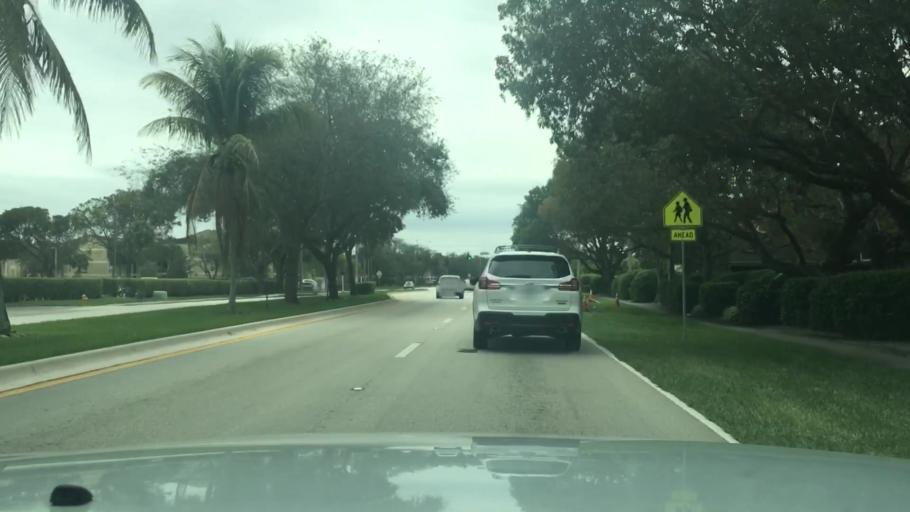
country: US
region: Florida
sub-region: Broward County
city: North Lauderdale
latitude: 26.2444
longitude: -80.2430
